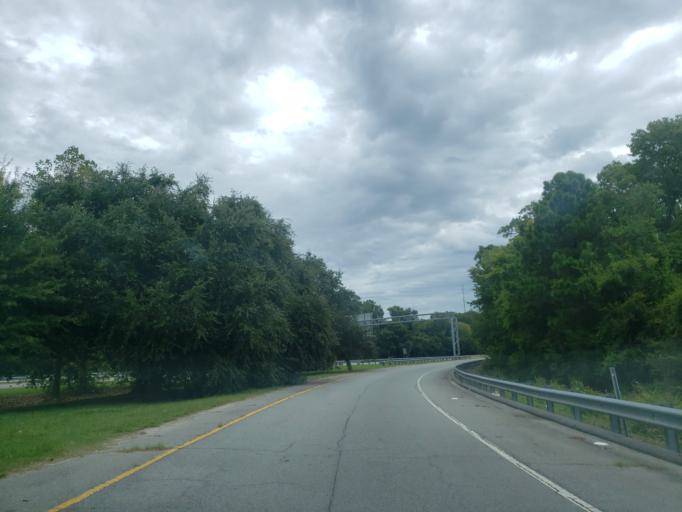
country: US
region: Georgia
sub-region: Chatham County
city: Thunderbolt
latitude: 32.0353
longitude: -81.0810
